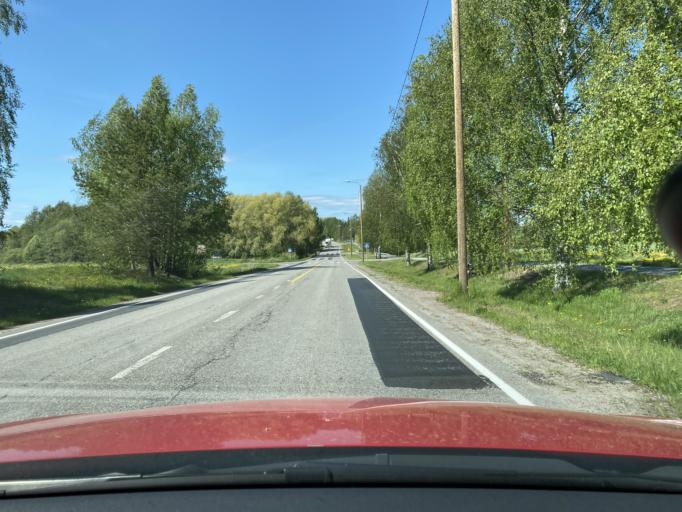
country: FI
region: Satakunta
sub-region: Rauma
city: Eura
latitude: 61.1157
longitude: 22.1536
